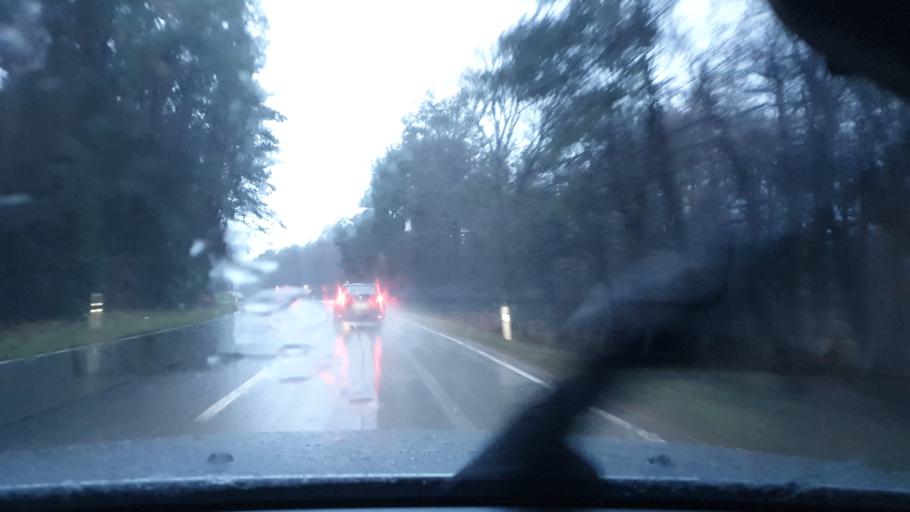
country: DE
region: Rheinland-Pfalz
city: Bechhofen
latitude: 49.3662
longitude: 7.3783
